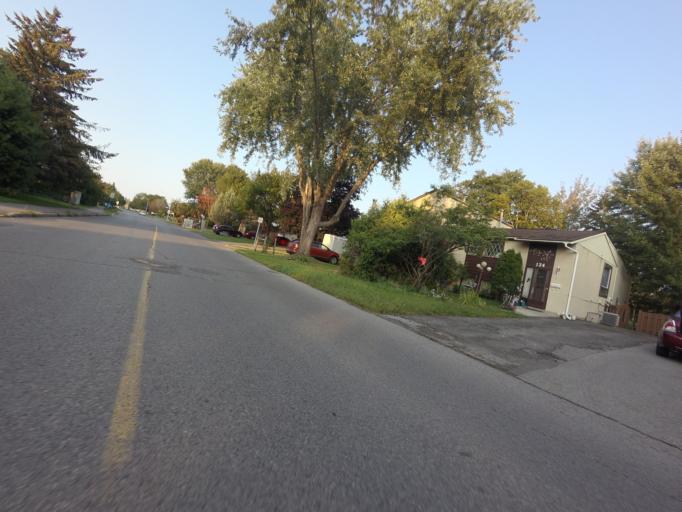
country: CA
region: Ontario
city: Bells Corners
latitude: 45.2888
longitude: -75.8746
